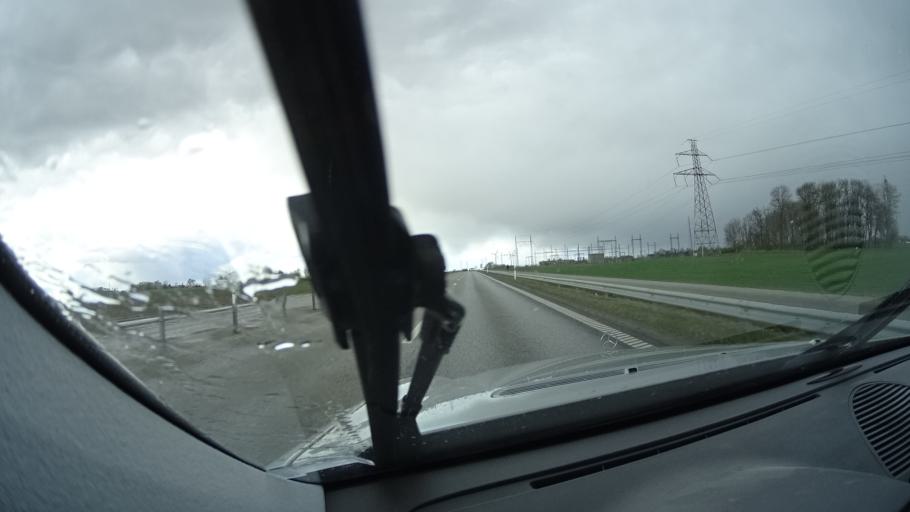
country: SE
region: Skane
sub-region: Lunds Kommun
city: Lund
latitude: 55.7373
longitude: 13.1445
